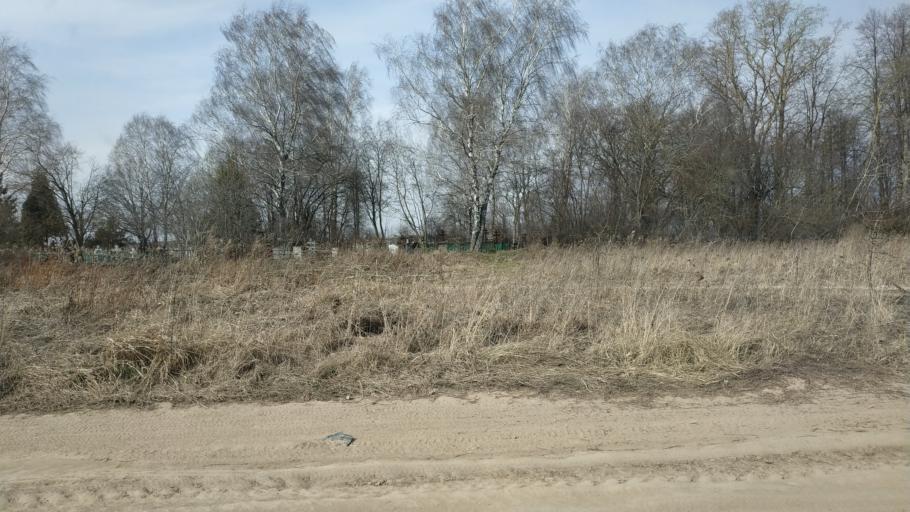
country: RU
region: Moskovskaya
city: Troitskoye
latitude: 55.3560
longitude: 38.4859
